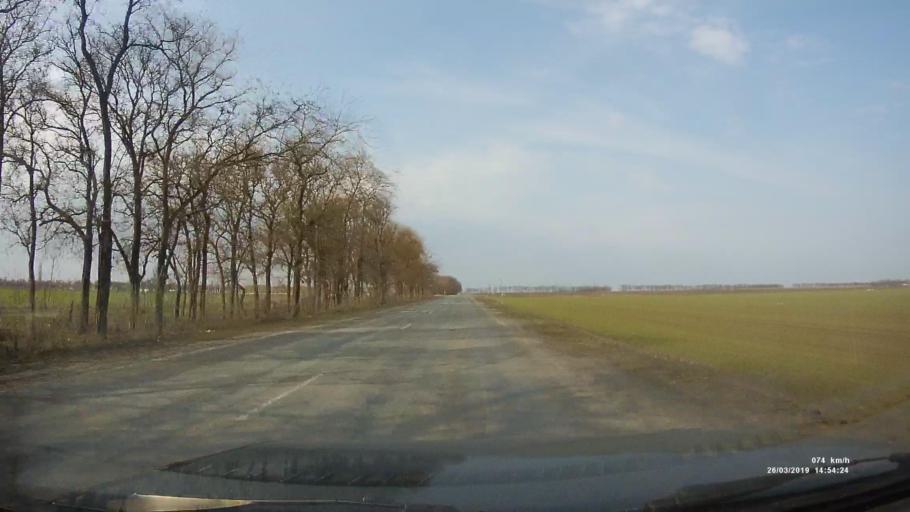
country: RU
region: Rostov
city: Novobessergenovka
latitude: 47.1933
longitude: 38.8135
